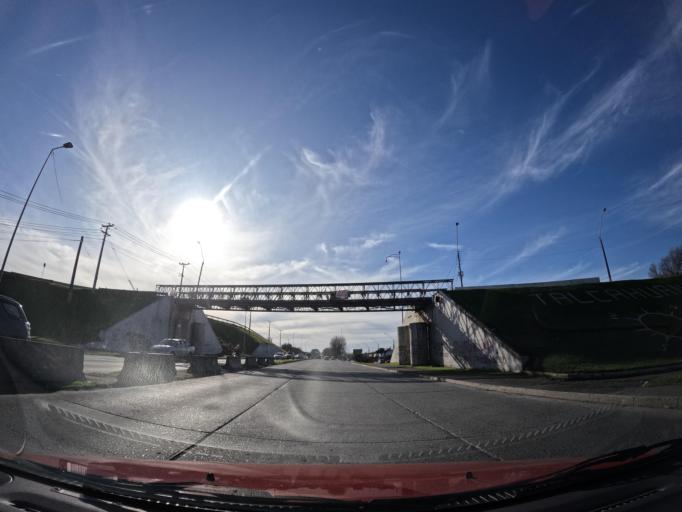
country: CL
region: Biobio
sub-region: Provincia de Concepcion
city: Talcahuano
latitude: -36.7673
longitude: -73.0847
